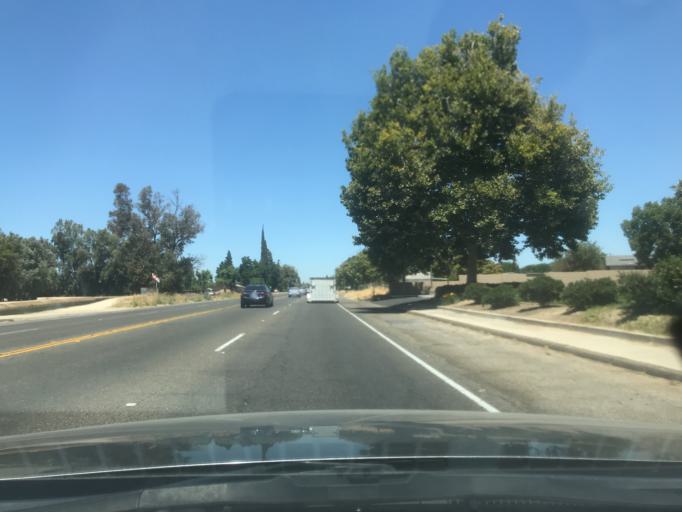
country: US
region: California
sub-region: Merced County
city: Atwater
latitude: 37.3681
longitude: -120.6138
